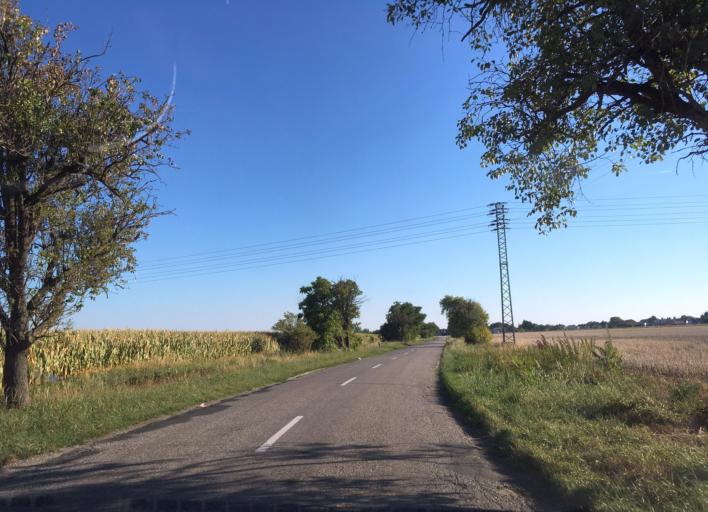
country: SK
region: Trnavsky
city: Samorin
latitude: 48.0270
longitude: 17.3345
